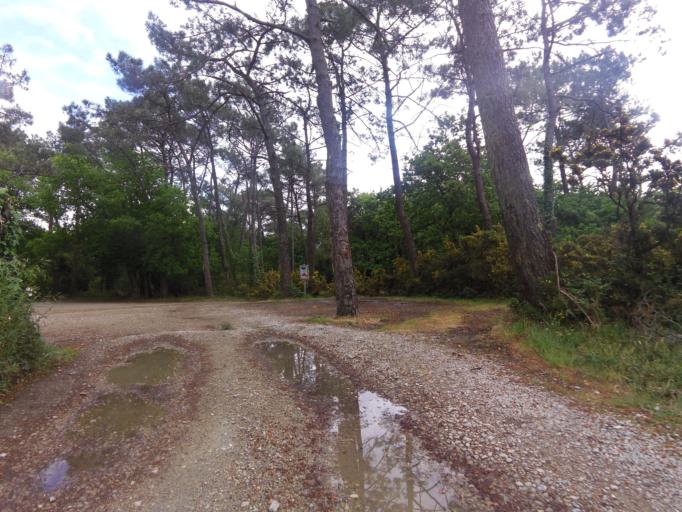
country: FR
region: Brittany
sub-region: Departement du Morbihan
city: Locmariaquer
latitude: 47.5962
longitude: -2.9391
